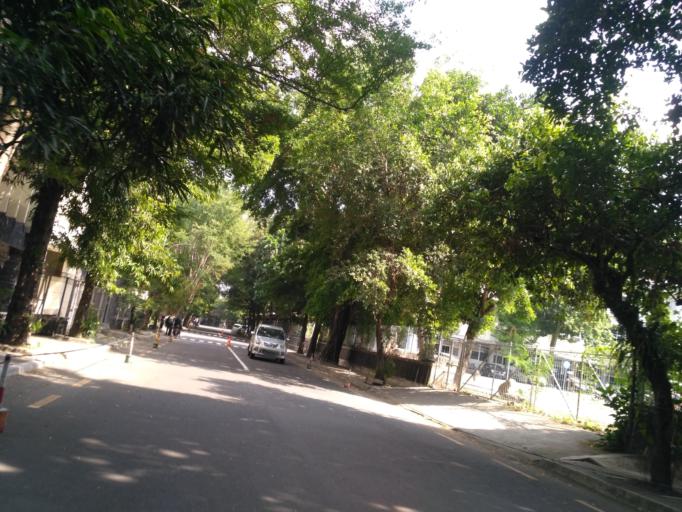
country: ID
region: Daerah Istimewa Yogyakarta
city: Yogyakarta
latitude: -7.7678
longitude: 110.3762
